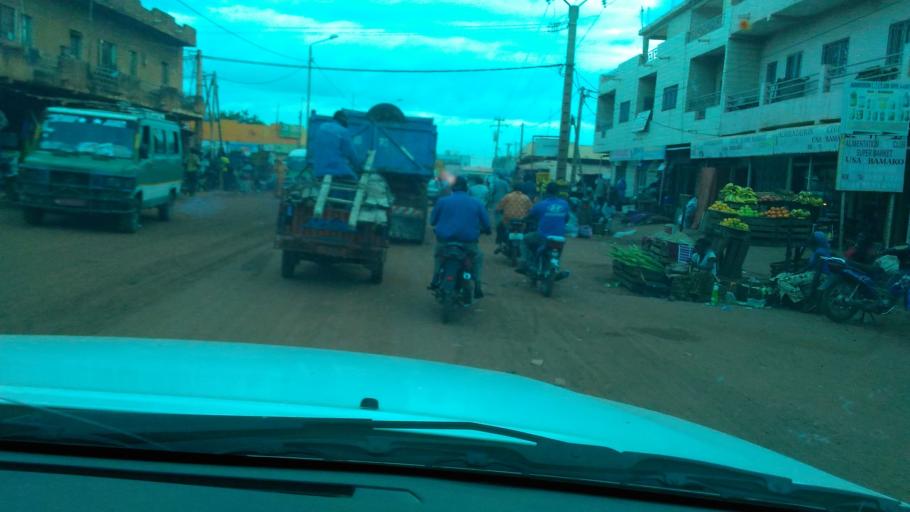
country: ML
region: Bamako
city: Bamako
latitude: 12.5744
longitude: -8.0273
